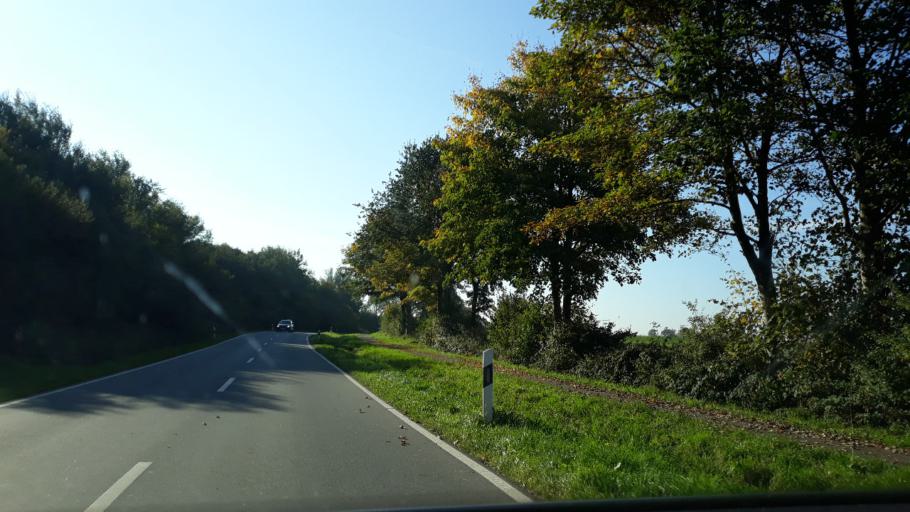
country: DE
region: Schleswig-Holstein
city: Boklund
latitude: 54.6123
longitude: 9.5873
